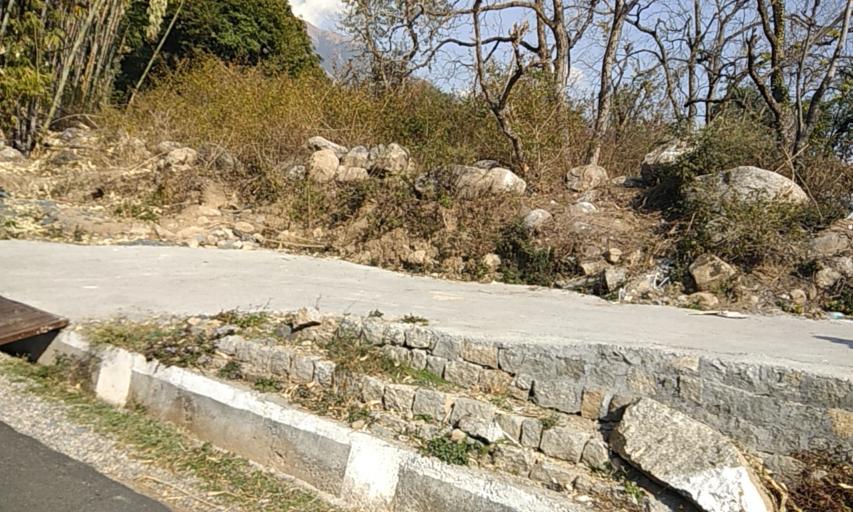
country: IN
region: Himachal Pradesh
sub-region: Kangra
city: Dharmsala
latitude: 32.1572
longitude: 76.4062
